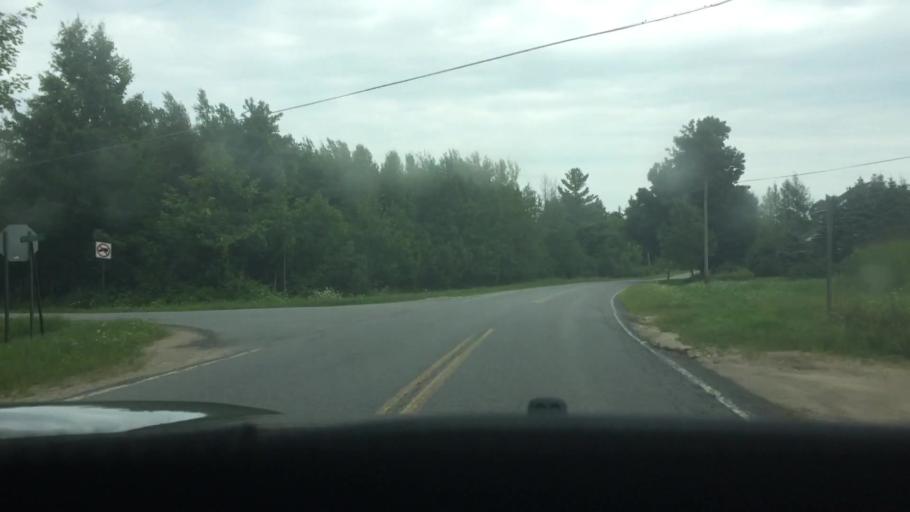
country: US
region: New York
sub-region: St. Lawrence County
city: Hannawa Falls
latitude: 44.6239
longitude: -74.8477
